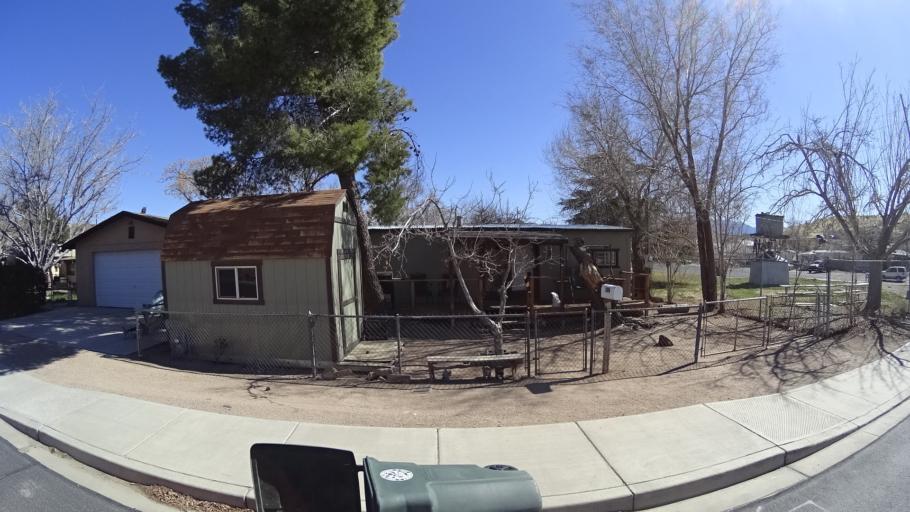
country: US
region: Arizona
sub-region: Mohave County
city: Kingman
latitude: 35.1858
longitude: -114.0534
